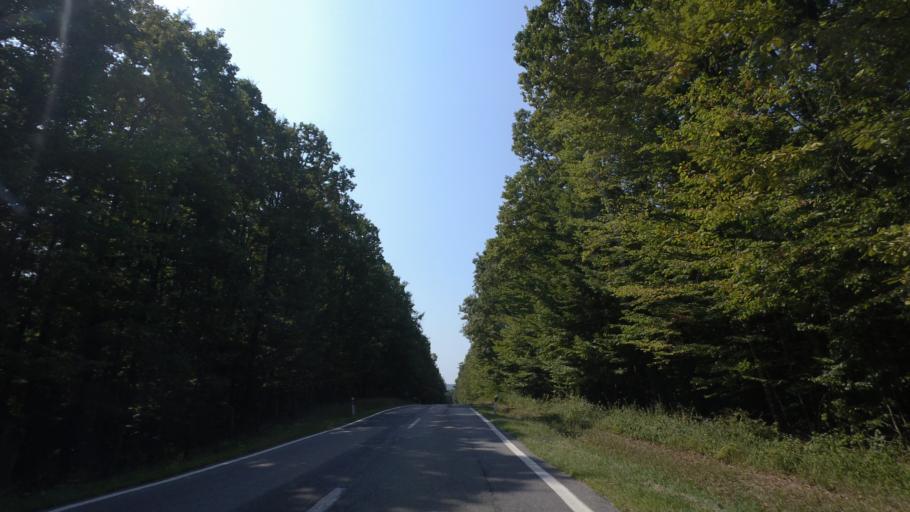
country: HR
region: Pozesko-Slavonska
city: Lipik
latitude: 45.4067
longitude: 17.0631
